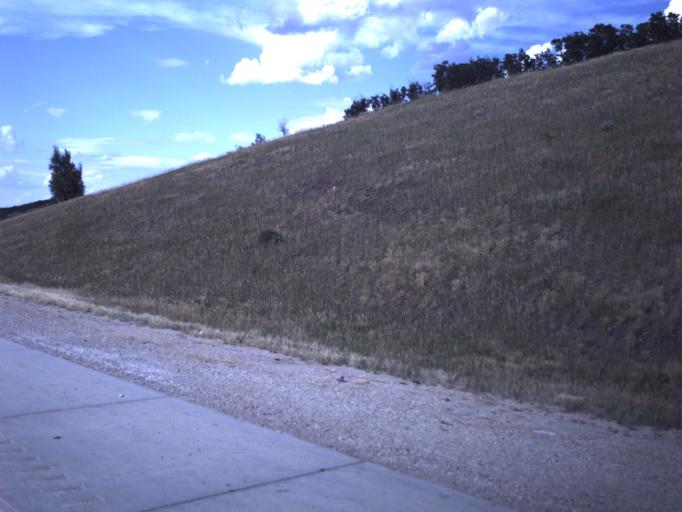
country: US
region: Utah
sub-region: Summit County
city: Park City
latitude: 40.6545
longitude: -111.4568
